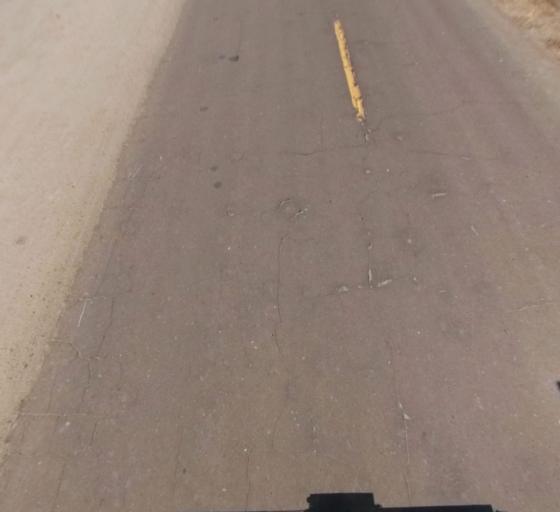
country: US
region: California
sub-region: Fresno County
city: Biola
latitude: 36.8252
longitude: -120.0247
